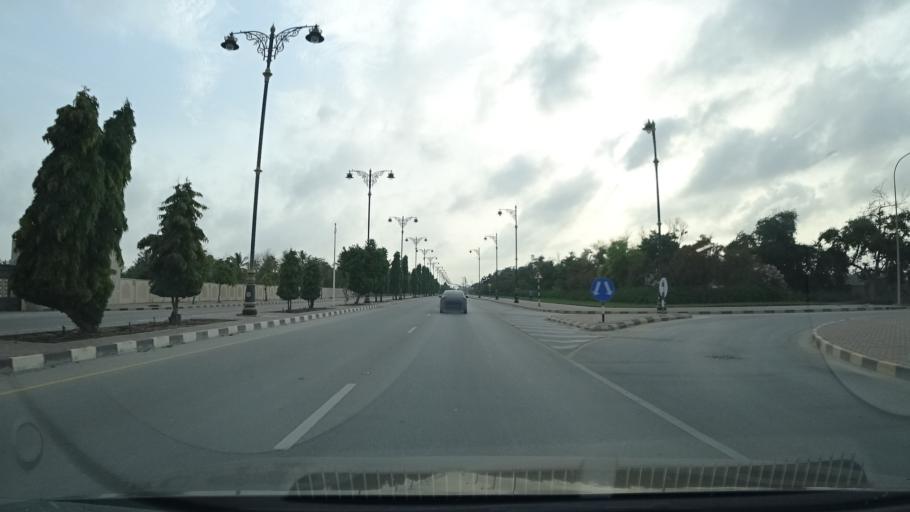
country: OM
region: Zufar
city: Salalah
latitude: 17.0260
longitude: 54.1670
